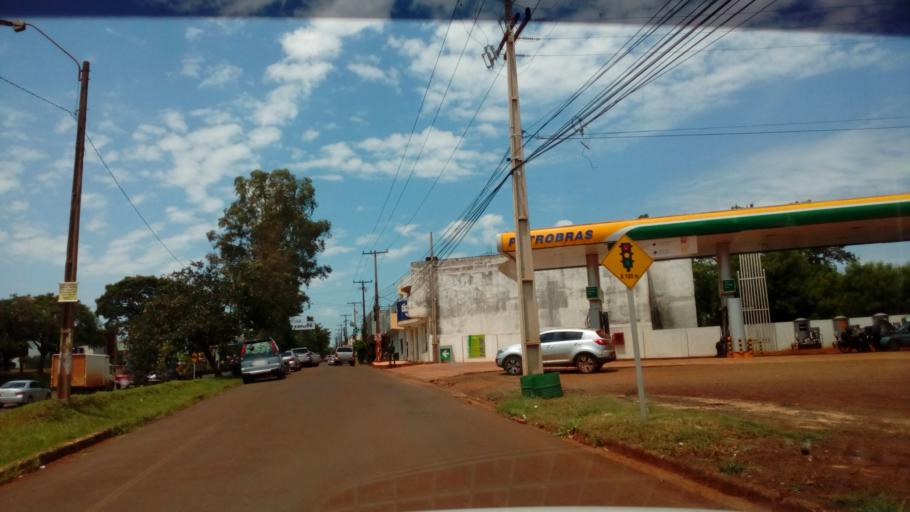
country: PY
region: Alto Parana
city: Santa Rita
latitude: -25.7925
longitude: -55.0862
